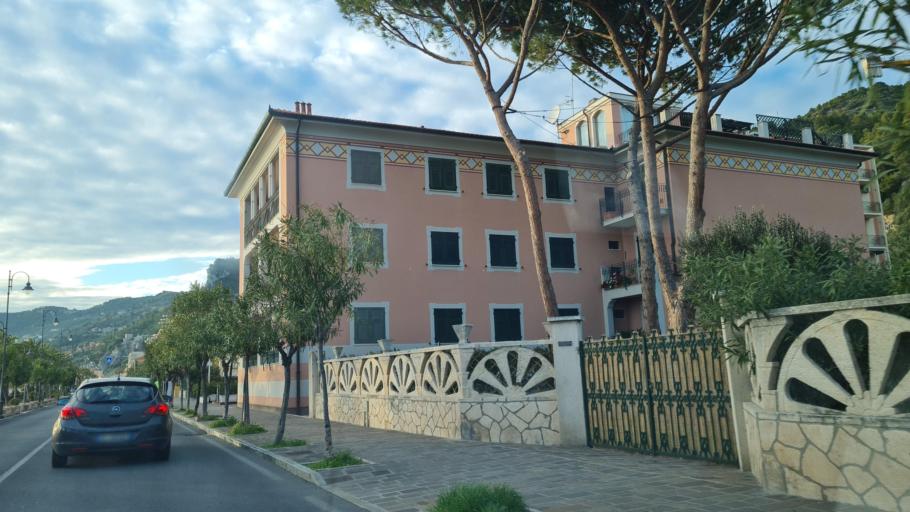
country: IT
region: Liguria
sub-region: Provincia di Savona
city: Noli
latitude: 44.1817
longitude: 8.3963
